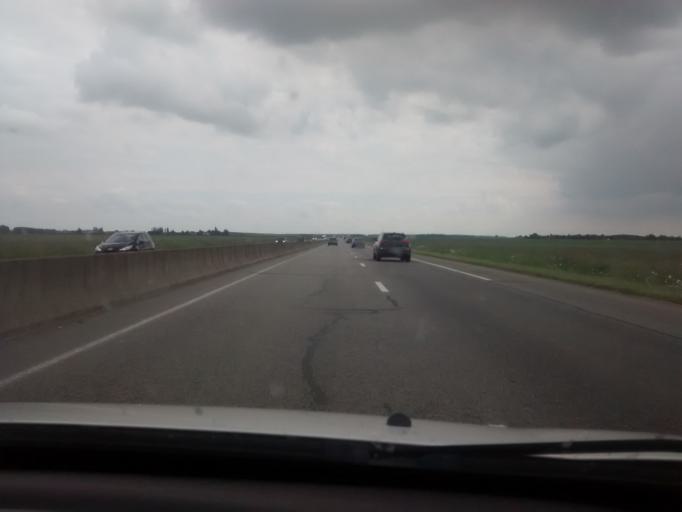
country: FR
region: Ile-de-France
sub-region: Departement des Yvelines
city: Sonchamp
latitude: 48.5978
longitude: 1.8318
